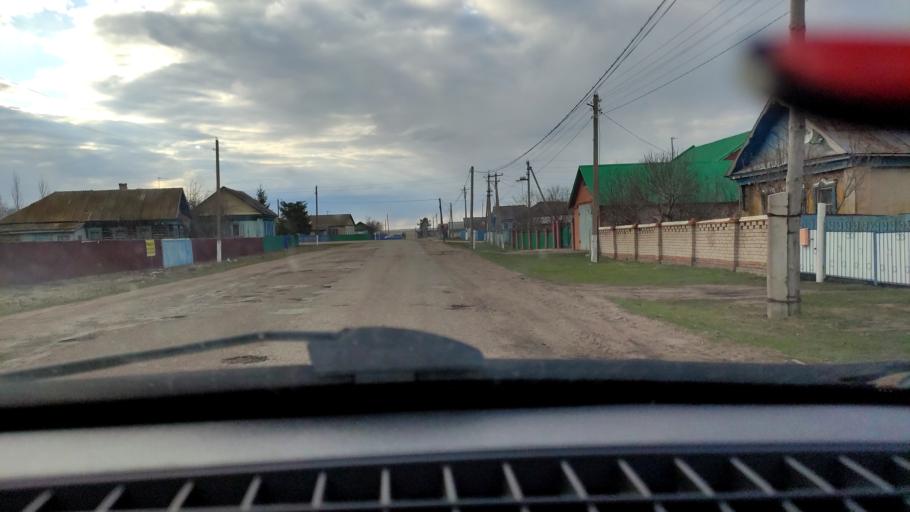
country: RU
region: Bashkortostan
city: Karmaskaly
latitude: 54.3355
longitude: 56.0006
